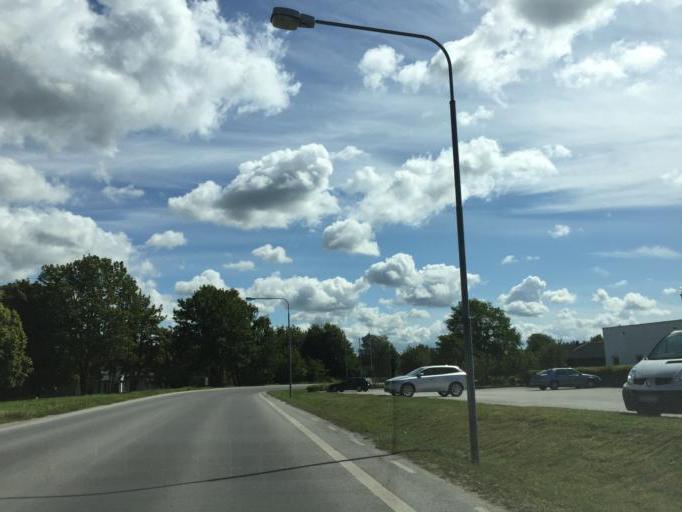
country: SE
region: Gotland
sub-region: Gotland
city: Visby
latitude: 57.6158
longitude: 18.2842
